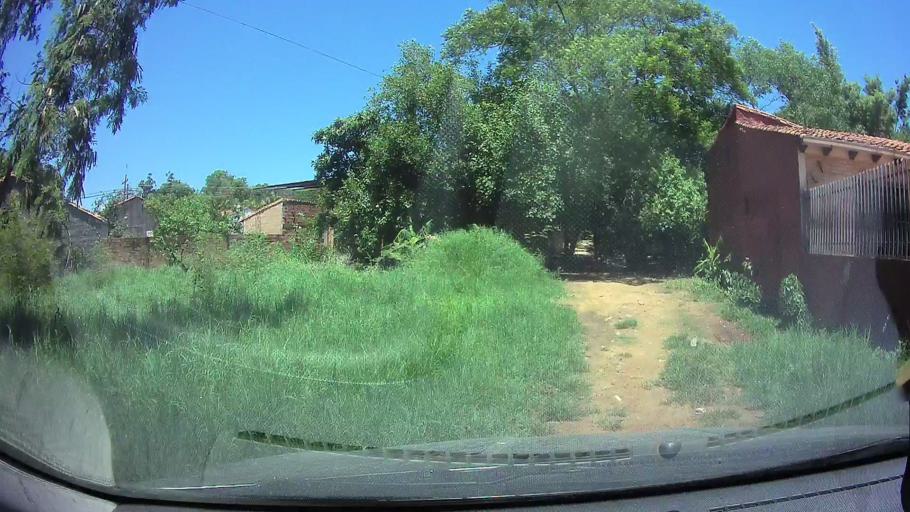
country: PY
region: Central
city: San Lorenzo
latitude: -25.3484
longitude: -57.4901
